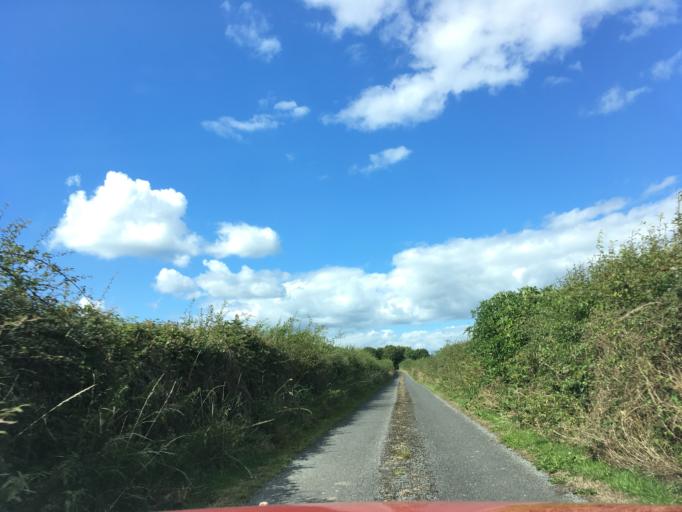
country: IE
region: Munster
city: Cashel
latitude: 52.4593
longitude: -7.9416
